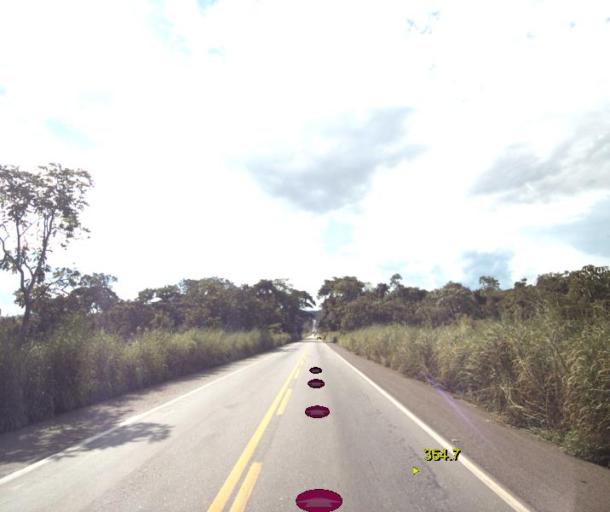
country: BR
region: Goias
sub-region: Jaragua
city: Jaragua
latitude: -15.6951
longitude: -49.3364
